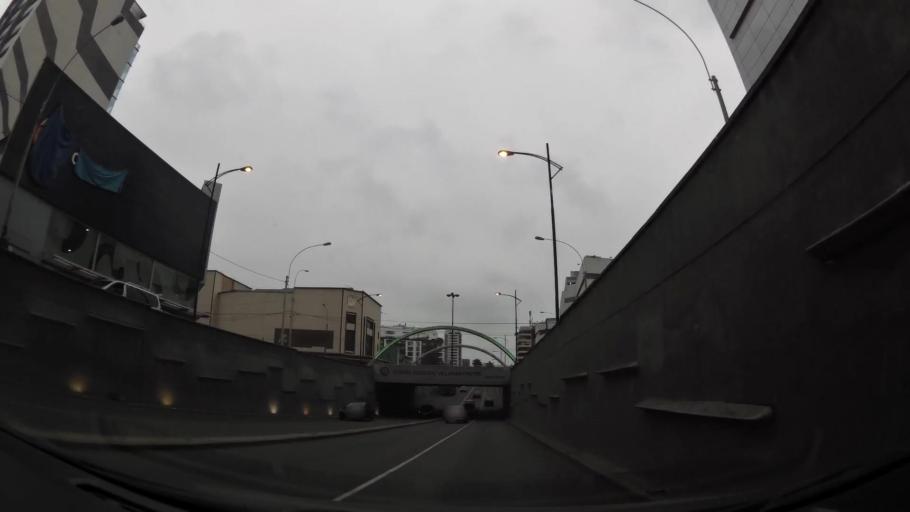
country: PE
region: Lima
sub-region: Lima
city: San Isidro
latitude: -12.0918
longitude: -77.0334
